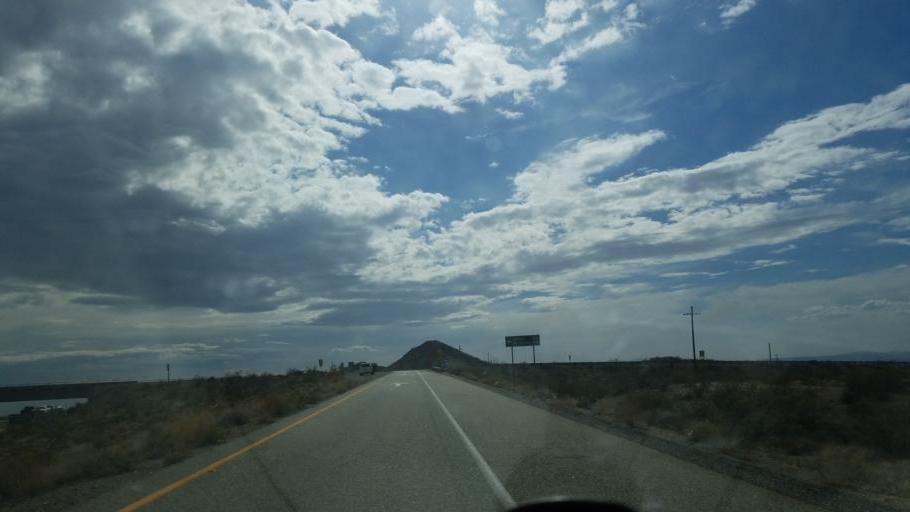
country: US
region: California
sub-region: San Bernardino County
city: Needles
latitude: 34.8311
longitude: -115.0496
